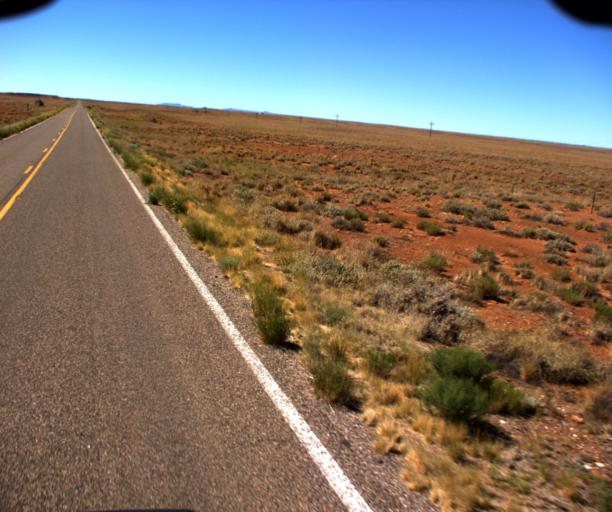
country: US
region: Arizona
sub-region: Coconino County
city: LeChee
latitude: 35.2200
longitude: -110.9529
